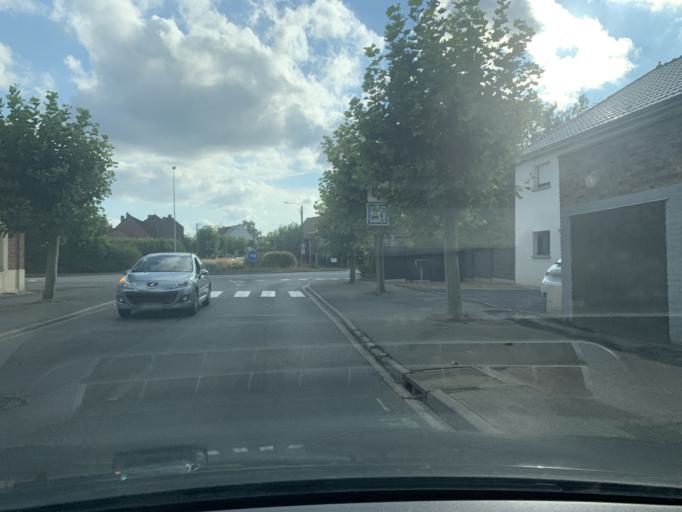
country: FR
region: Nord-Pas-de-Calais
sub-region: Departement du Pas-de-Calais
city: Dourges
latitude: 50.4392
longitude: 2.9929
